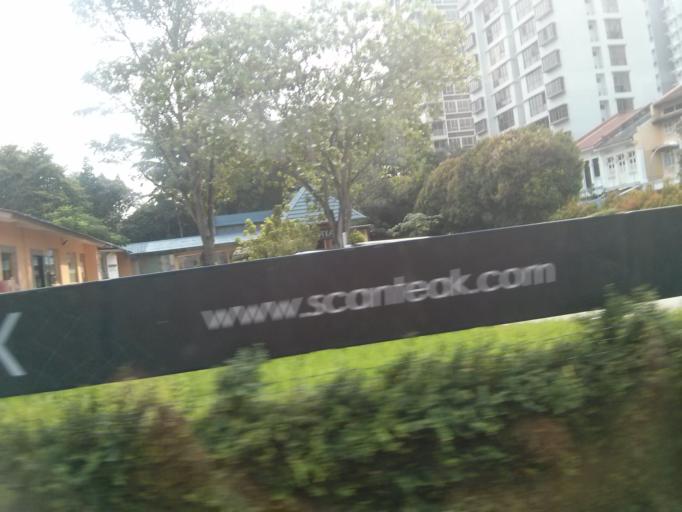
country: SG
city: Singapore
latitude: 1.3234
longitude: 103.8520
